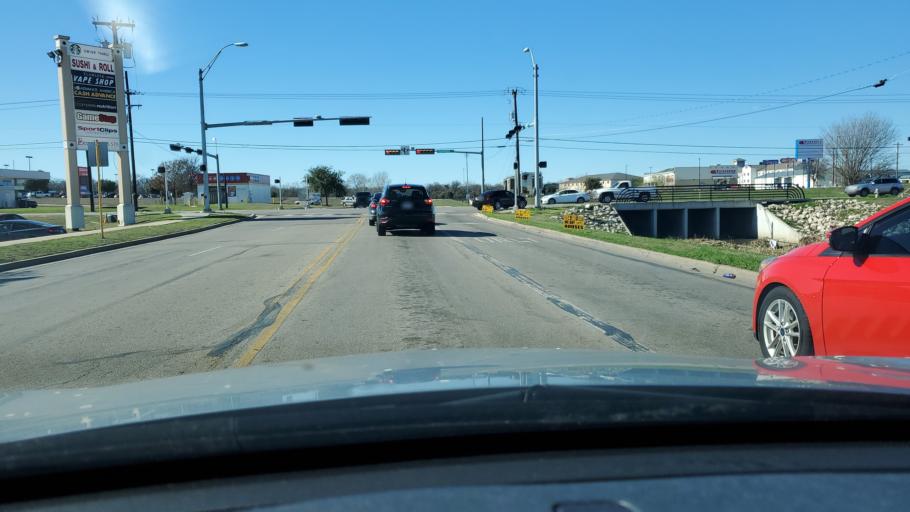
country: US
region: Texas
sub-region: Bell County
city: Killeen
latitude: 31.0923
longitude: -97.7326
